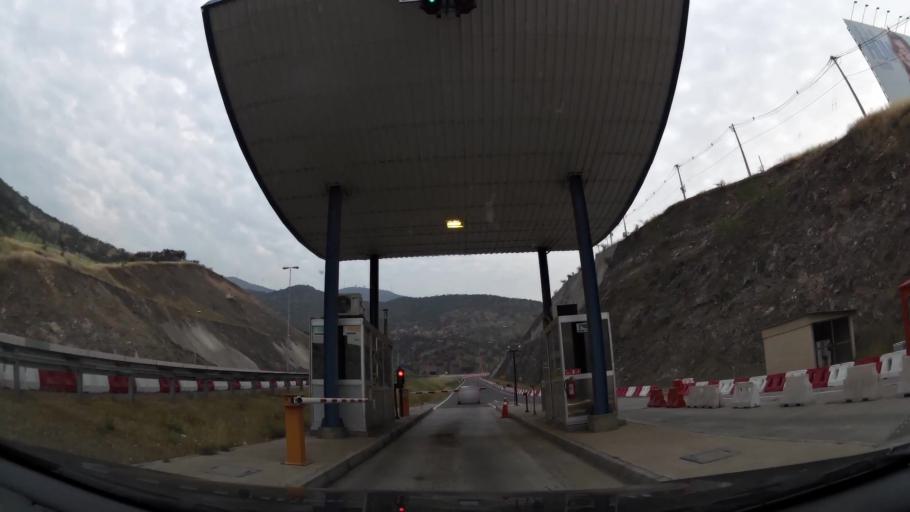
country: CL
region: Santiago Metropolitan
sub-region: Provincia de Chacabuco
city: Chicureo Abajo
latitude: -33.3244
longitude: -70.6248
